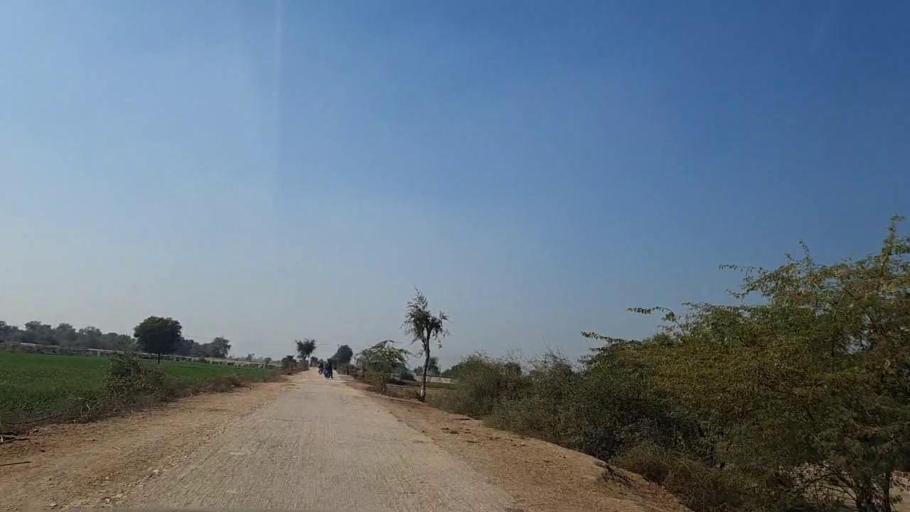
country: PK
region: Sindh
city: Daulatpur
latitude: 26.2906
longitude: 68.0821
